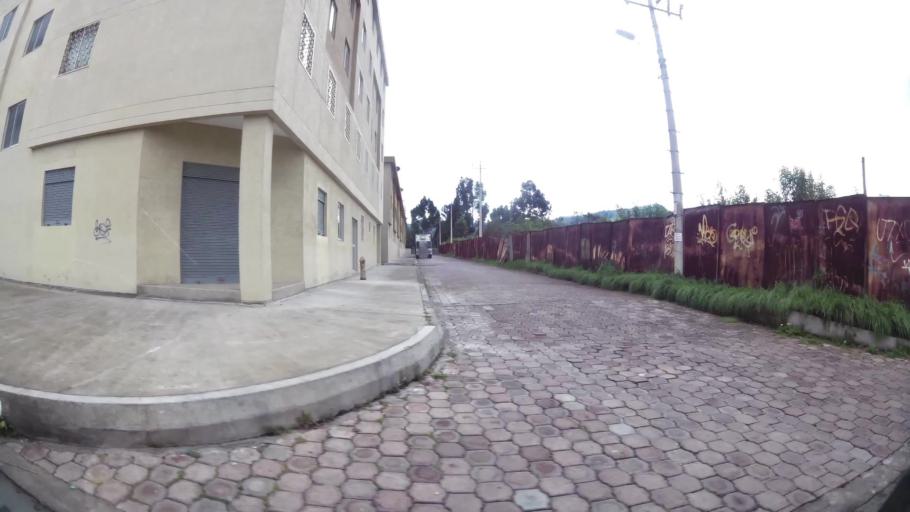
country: EC
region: Pichincha
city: Quito
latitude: -0.2958
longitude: -78.5522
